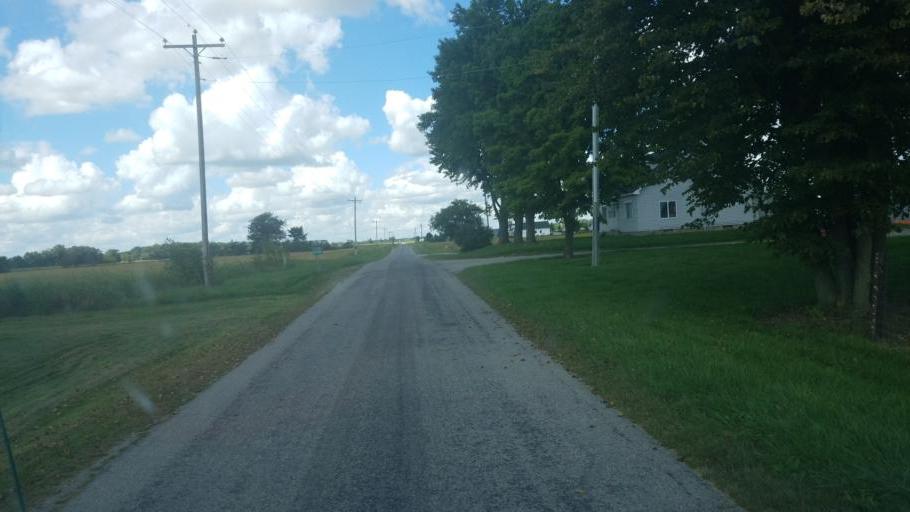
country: US
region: Ohio
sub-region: Union County
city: Richwood
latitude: 40.4531
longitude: -83.4940
